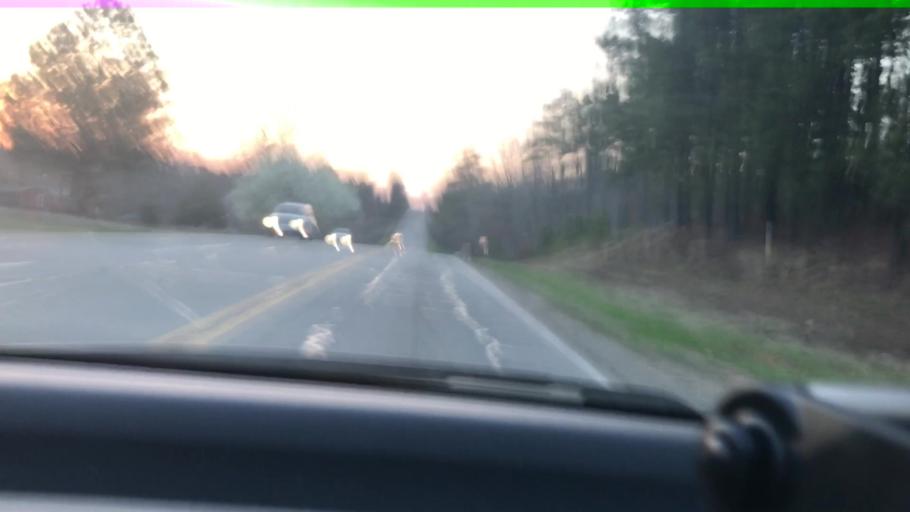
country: US
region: Georgia
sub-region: Oglethorpe County
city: Lexington
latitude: 33.8873
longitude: -83.1783
